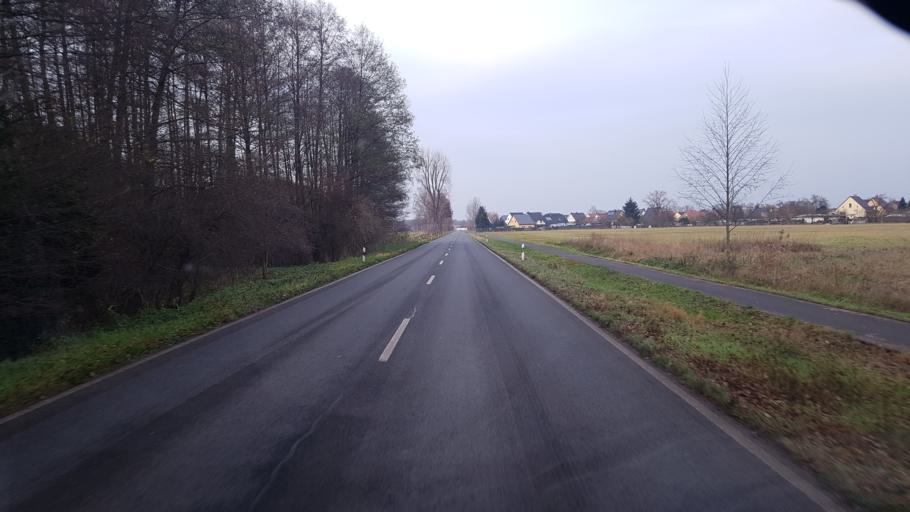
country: DE
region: Brandenburg
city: Vogelsang
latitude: 52.1740
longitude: 14.6678
